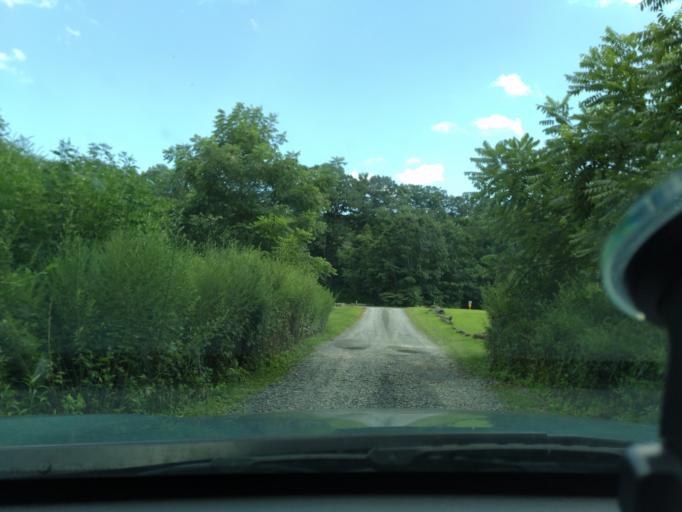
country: US
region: Pennsylvania
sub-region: Pike County
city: Birchwood Lakes
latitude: 41.2090
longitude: -74.8701
